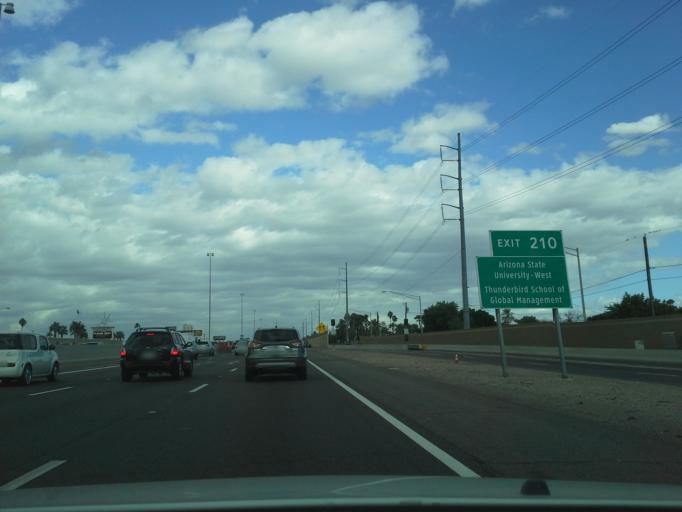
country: US
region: Arizona
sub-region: Maricopa County
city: Glendale
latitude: 33.5986
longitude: -112.1167
